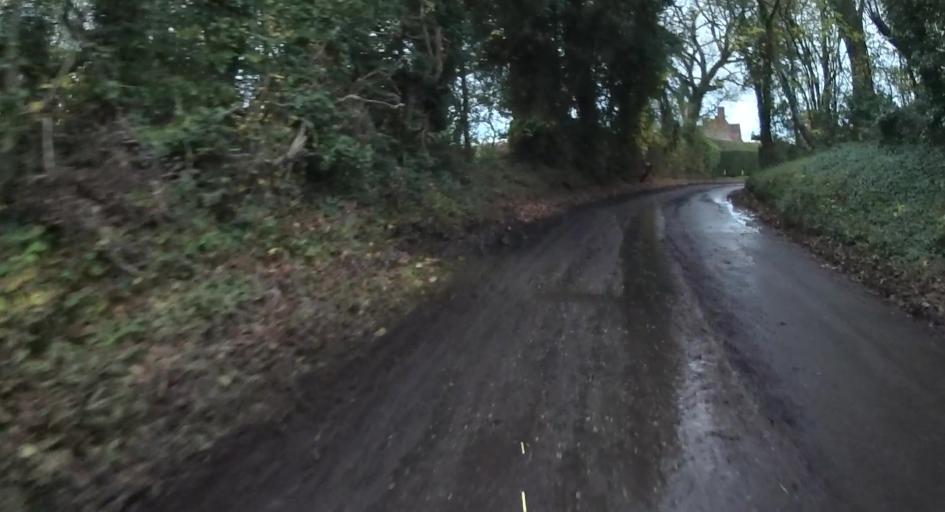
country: GB
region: England
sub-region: Hampshire
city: Long Sutton
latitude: 51.2149
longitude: -0.9102
